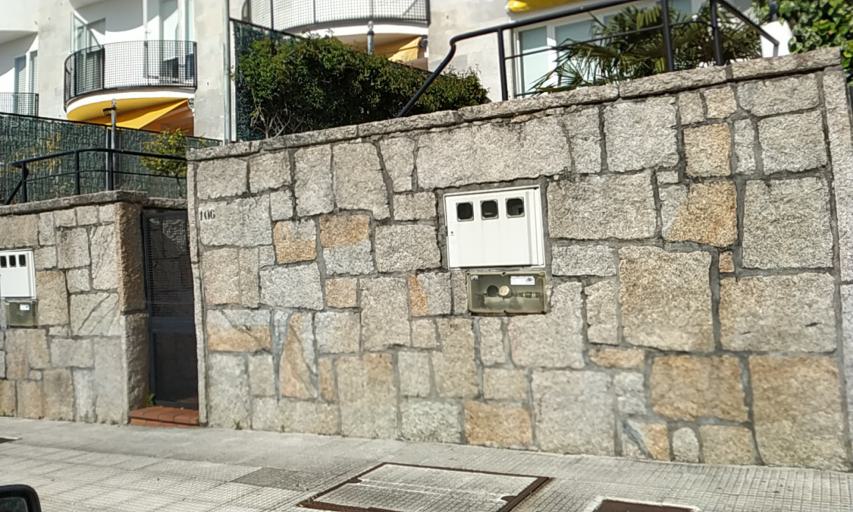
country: ES
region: Galicia
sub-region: Provincia de Pontevedra
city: Sanxenxo
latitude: 42.3998
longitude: -8.8188
